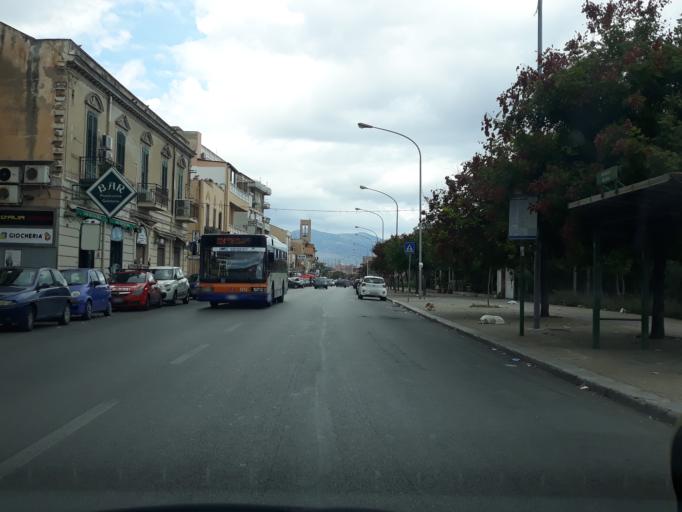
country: IT
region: Sicily
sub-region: Palermo
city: Ciaculli
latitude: 38.1042
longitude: 13.3911
